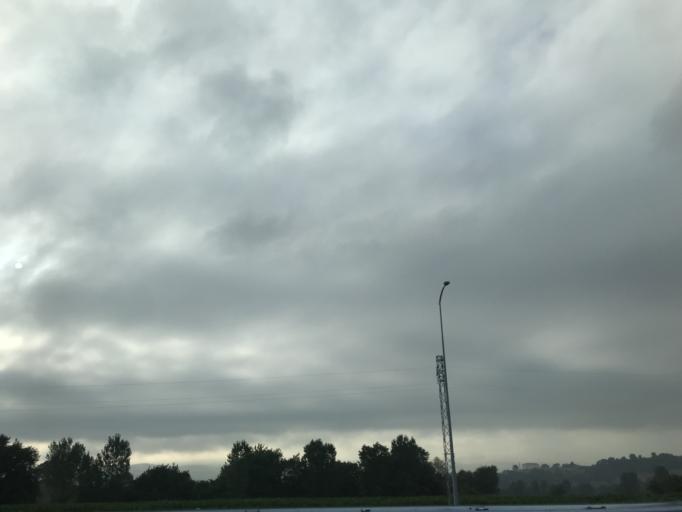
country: TR
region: Balikesir
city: Susurluk
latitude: 39.9263
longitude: 28.1348
